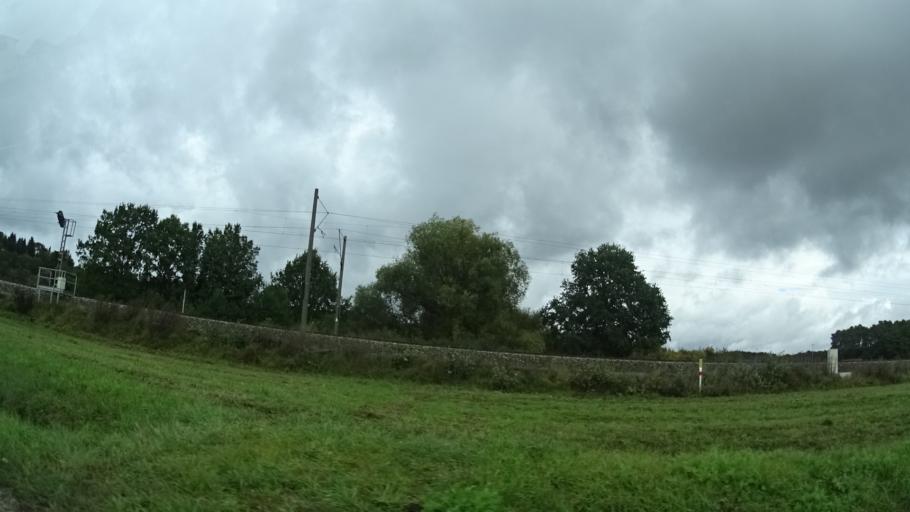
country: DE
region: Bavaria
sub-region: Upper Franconia
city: Oberhaid
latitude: 49.9346
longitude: 10.7963
